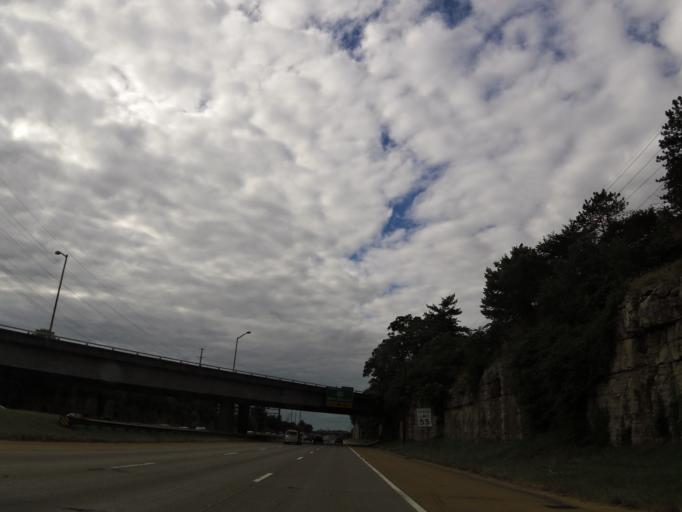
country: US
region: Tennessee
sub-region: Davidson County
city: Nashville
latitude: 36.1290
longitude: -86.8160
